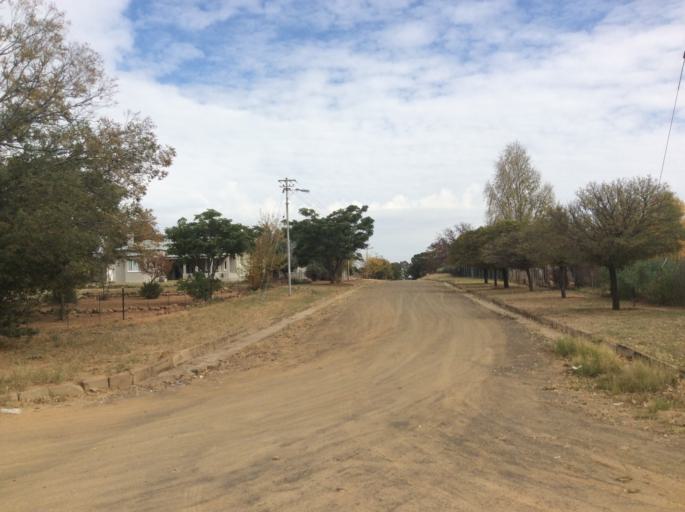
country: LS
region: Mafeteng
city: Mafeteng
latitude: -29.7303
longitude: 27.0323
